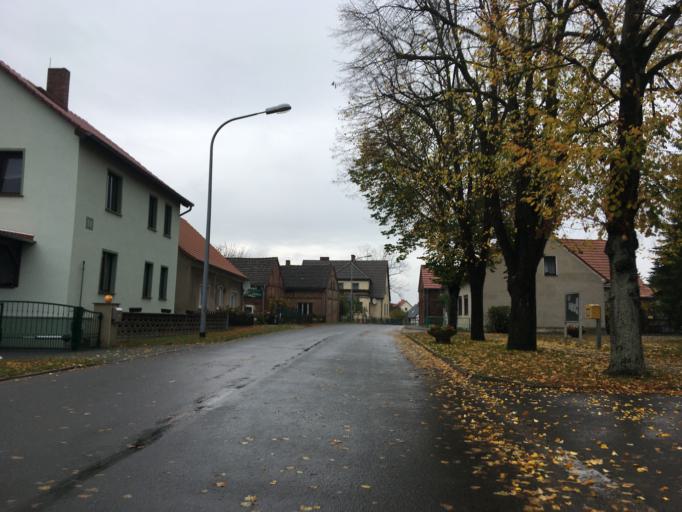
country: DE
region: Brandenburg
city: Friedland
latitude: 52.0406
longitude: 14.1811
